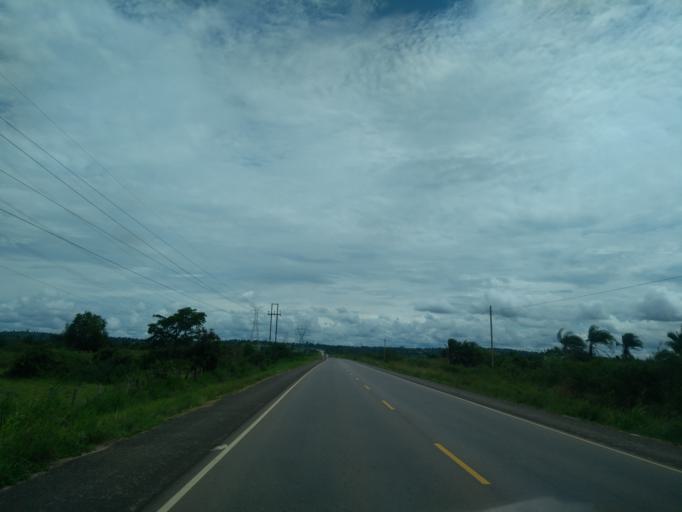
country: UG
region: Central Region
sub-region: Butambala District
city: Gombe
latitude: -0.0295
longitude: 32.0139
